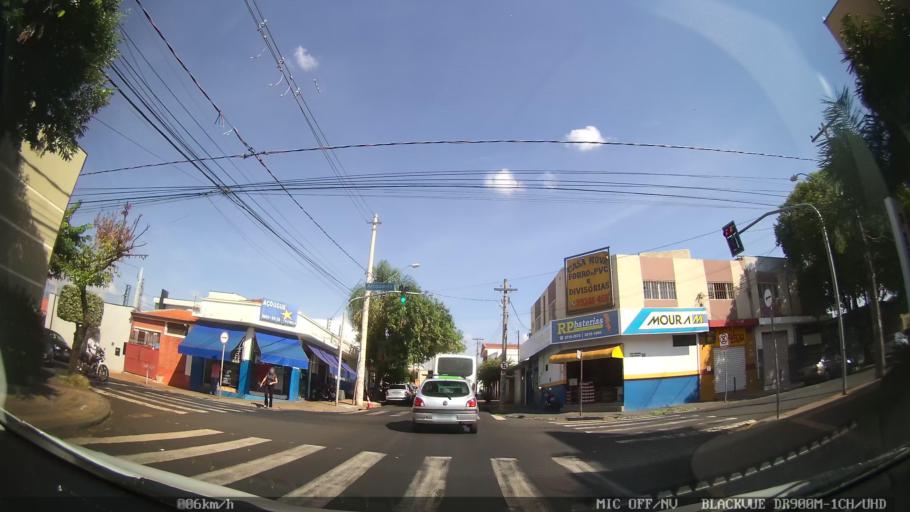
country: BR
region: Sao Paulo
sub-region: Ribeirao Preto
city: Ribeirao Preto
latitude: -21.1838
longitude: -47.8256
